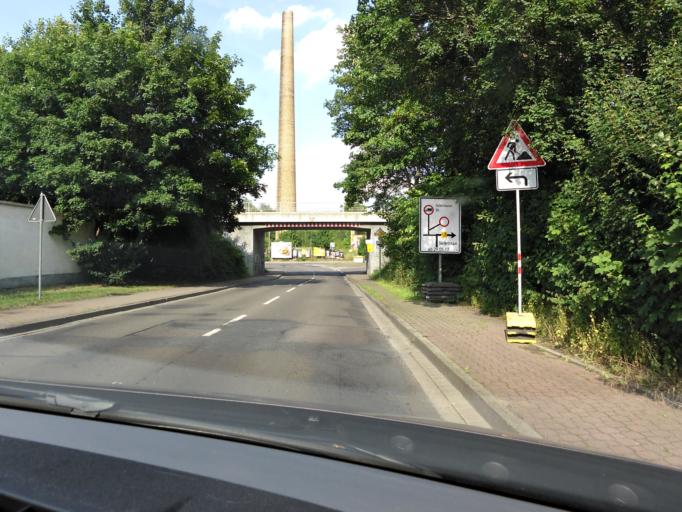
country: DE
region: Saxony
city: Grossposna
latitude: 51.2870
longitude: 12.4660
